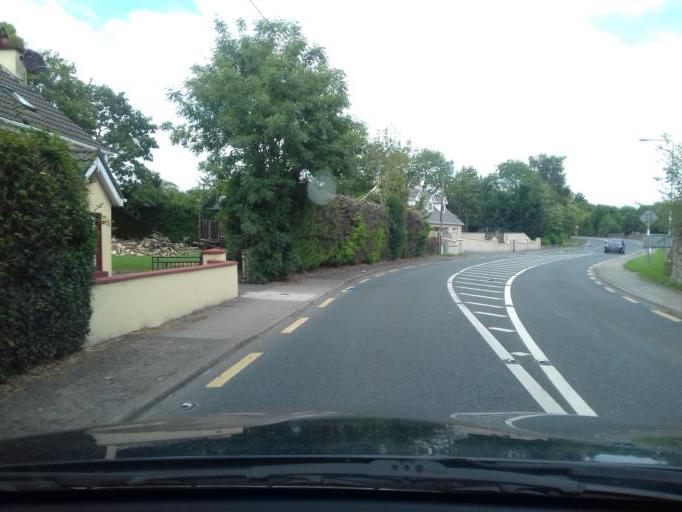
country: IE
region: Leinster
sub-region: County Carlow
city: Tullow
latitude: 52.8086
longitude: -6.7290
